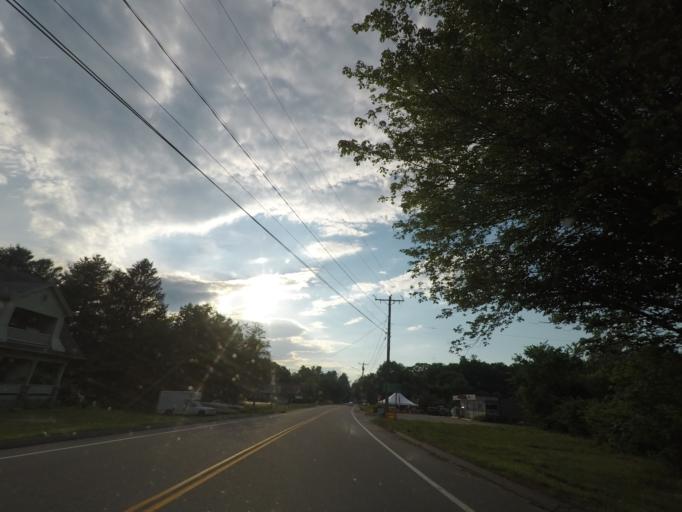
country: US
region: Connecticut
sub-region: Windham County
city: Quinebaug
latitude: 42.0244
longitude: -71.9509
